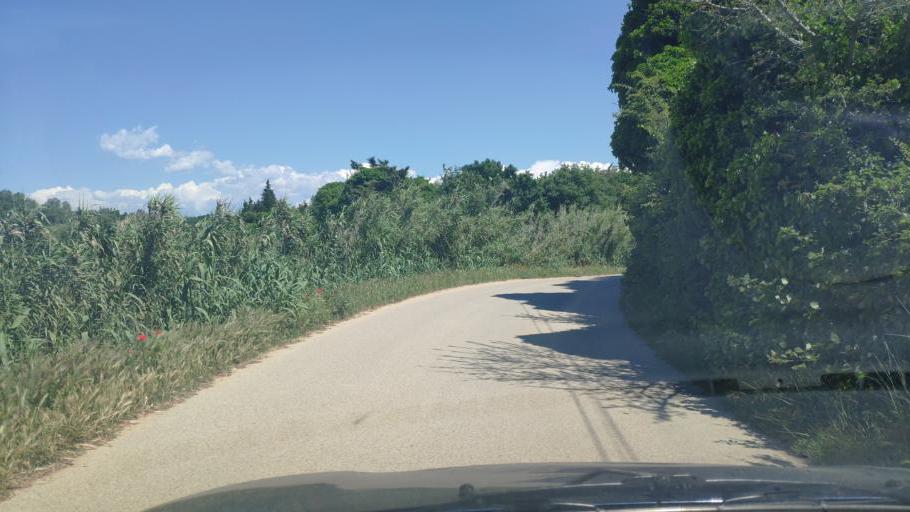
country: FR
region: Provence-Alpes-Cote d'Azur
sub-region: Departement du Vaucluse
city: Aubignan
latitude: 44.0781
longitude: 5.0242
